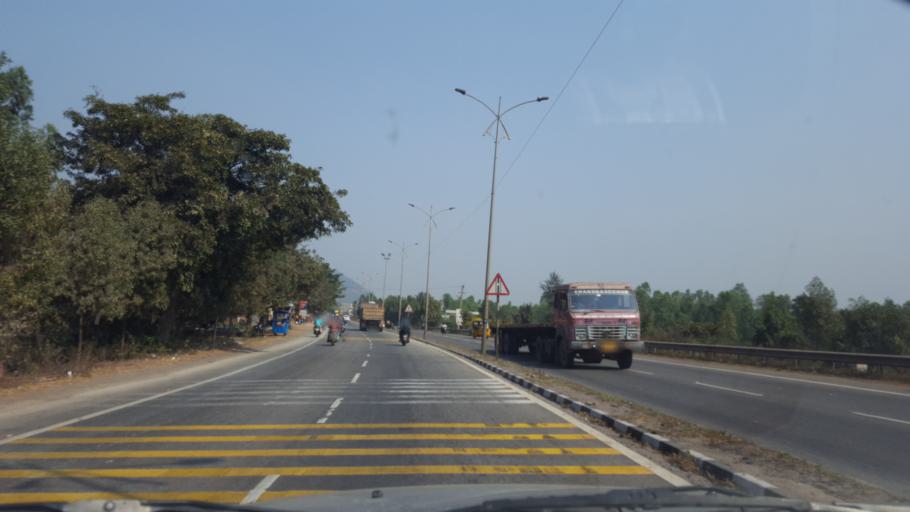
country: IN
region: Andhra Pradesh
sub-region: Vishakhapatnam
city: Anakapalle
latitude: 17.6886
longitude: 83.0692
